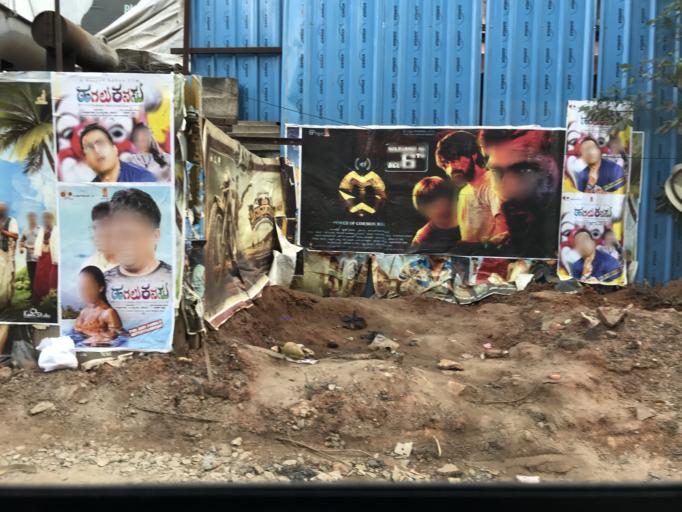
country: IN
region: Karnataka
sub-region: Bangalore Urban
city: Bangalore
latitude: 12.9756
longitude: 77.5772
